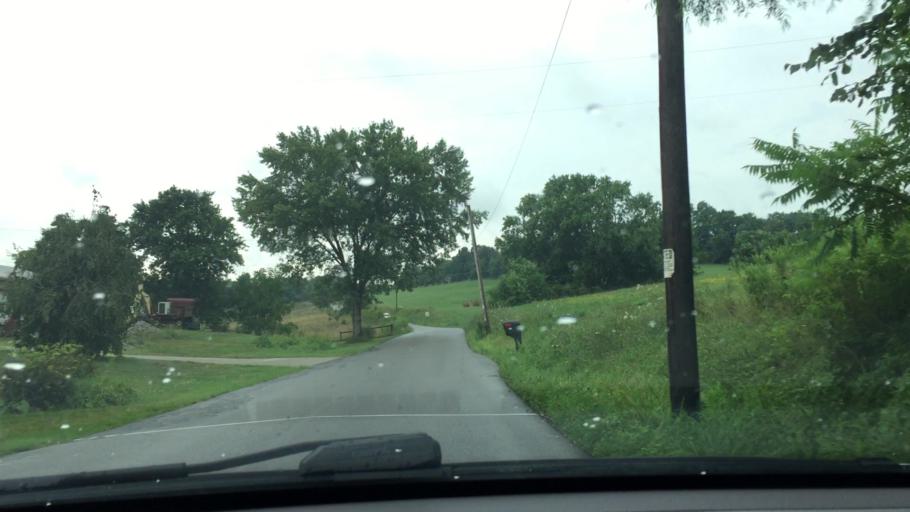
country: US
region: Pennsylvania
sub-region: Washington County
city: Muse
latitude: 40.2909
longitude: -80.1917
